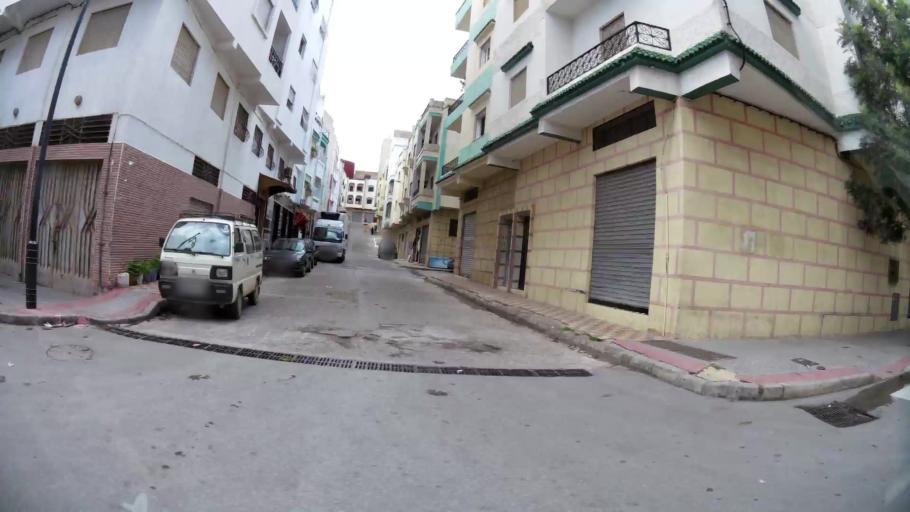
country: MA
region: Tanger-Tetouan
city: Tetouan
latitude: 35.5780
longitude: -5.3507
